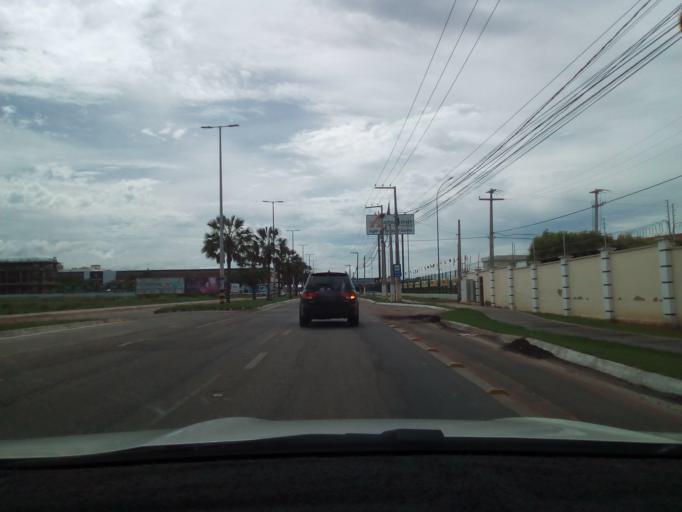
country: BR
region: Rio Grande do Norte
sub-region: Mossoro
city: Mossoro
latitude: -5.1729
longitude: -37.3730
